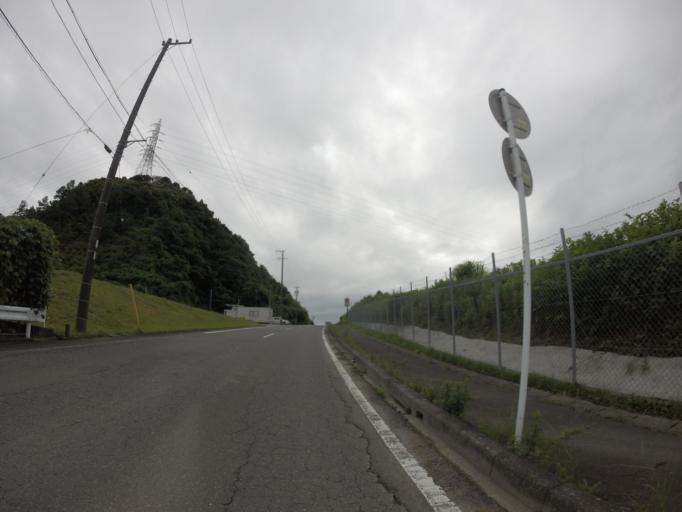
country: JP
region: Shizuoka
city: Sagara
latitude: 34.7277
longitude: 138.1708
